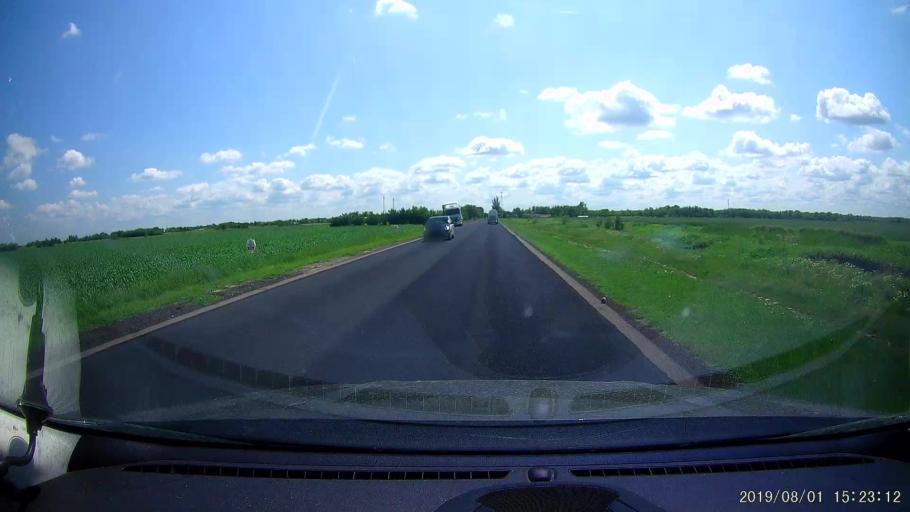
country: RO
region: Braila
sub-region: Comuna Viziru
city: Lanurile
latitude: 45.0435
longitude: 27.7633
